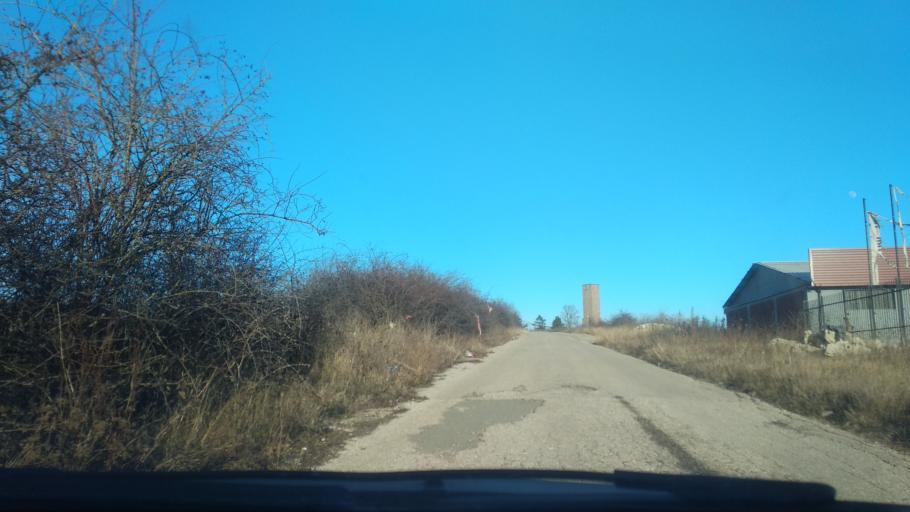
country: XK
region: Pristina
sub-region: Kosovo Polje
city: Kosovo Polje
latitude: 42.6888
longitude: 21.1196
